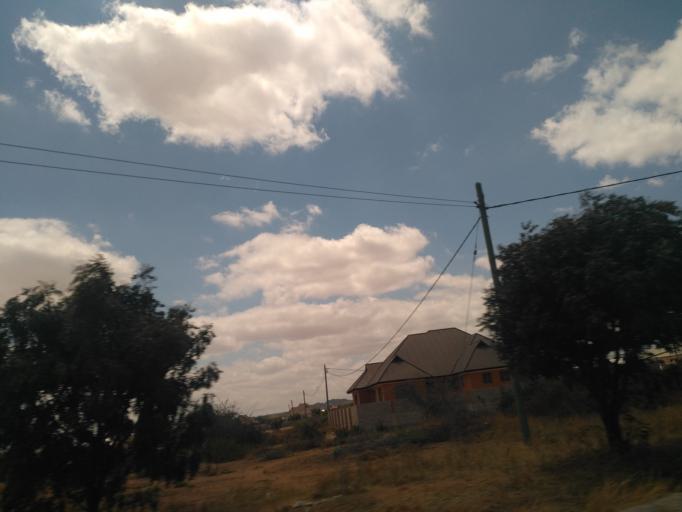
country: TZ
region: Dodoma
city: Kisasa
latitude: -6.1804
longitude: 35.7917
